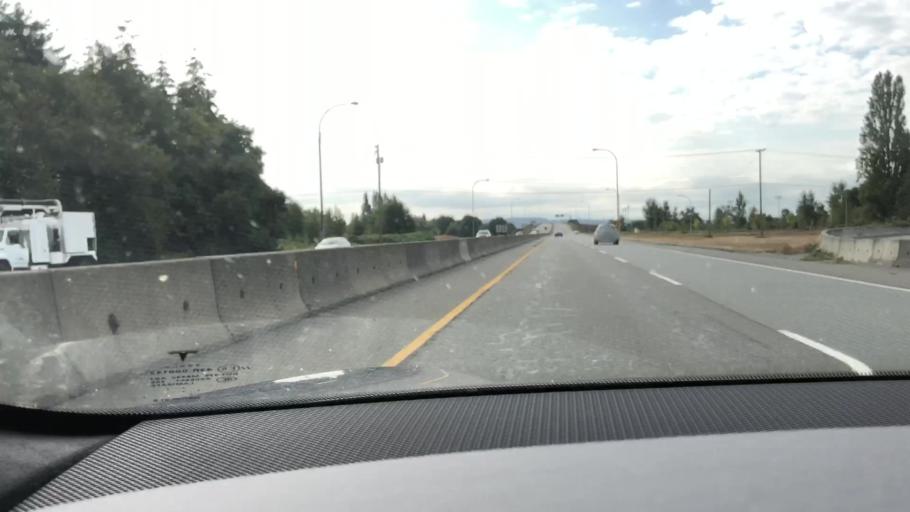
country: CA
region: British Columbia
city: Delta
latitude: 49.1012
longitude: -122.8998
